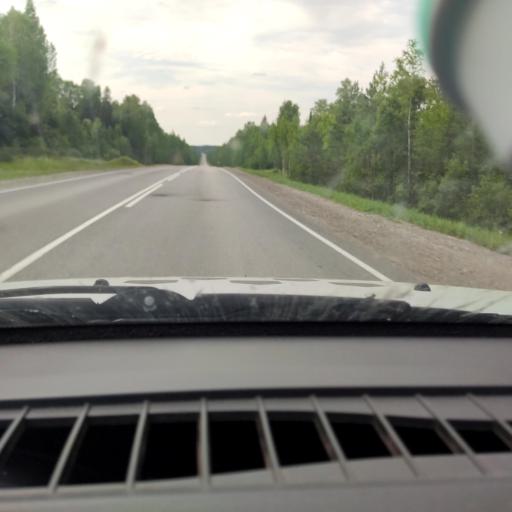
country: RU
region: Kirov
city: Chernaya Kholunitsa
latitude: 58.8323
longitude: 51.7589
